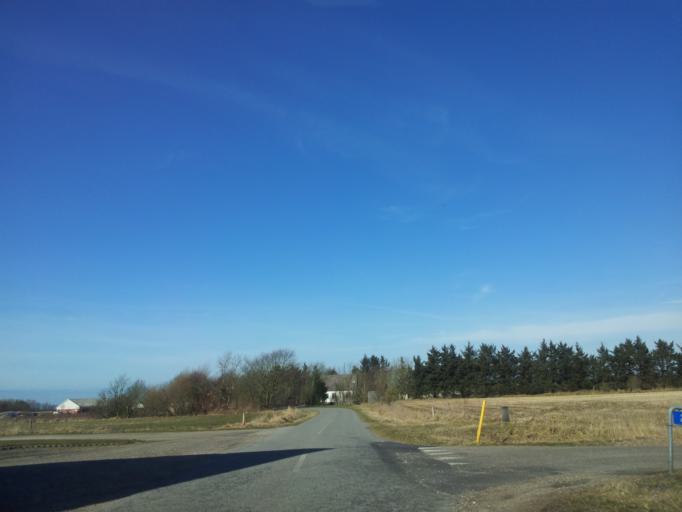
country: DK
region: South Denmark
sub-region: Tonder Kommune
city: Sherrebek
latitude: 55.1796
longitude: 8.7184
